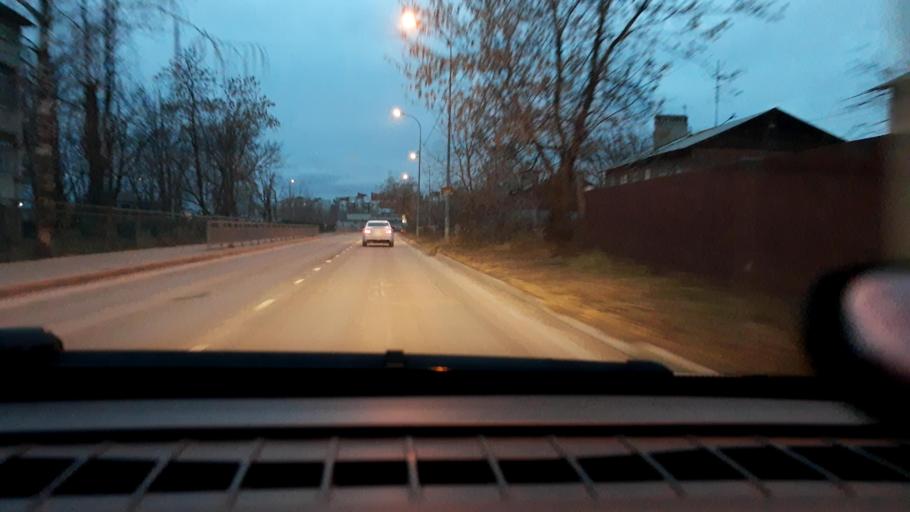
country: RU
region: Nizjnij Novgorod
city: Kstovo
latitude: 56.1390
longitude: 44.1972
